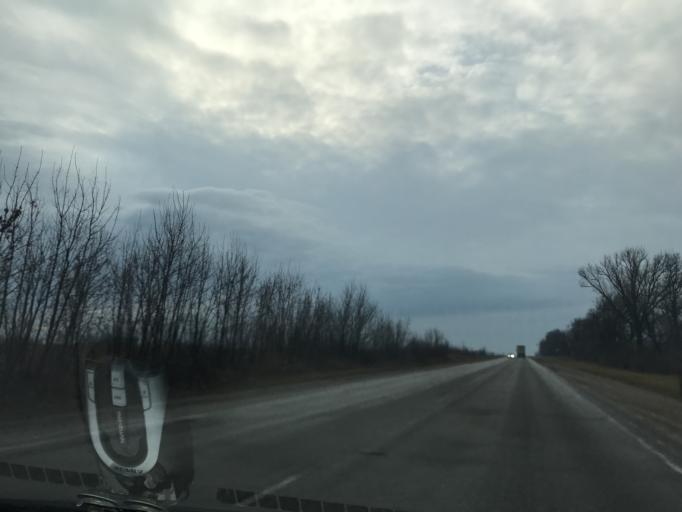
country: RU
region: Krasnodarskiy
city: Fastovetskaya
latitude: 45.9220
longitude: 40.0966
